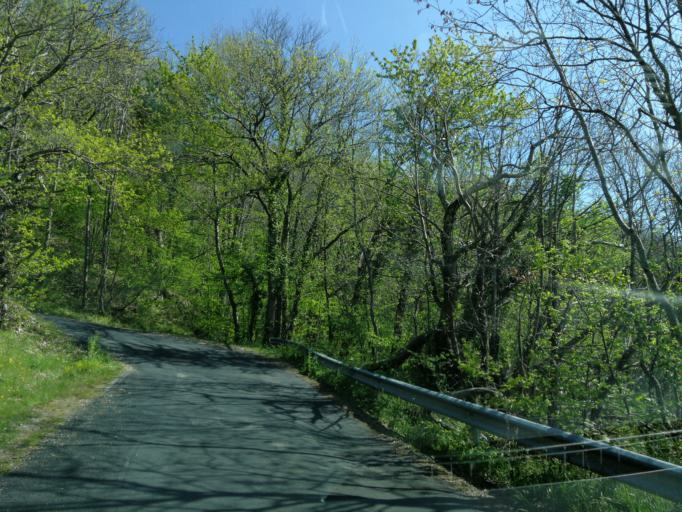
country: FR
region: Rhone-Alpes
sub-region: Departement de l'Ardeche
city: Le Cheylard
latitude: 44.9174
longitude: 4.4263
